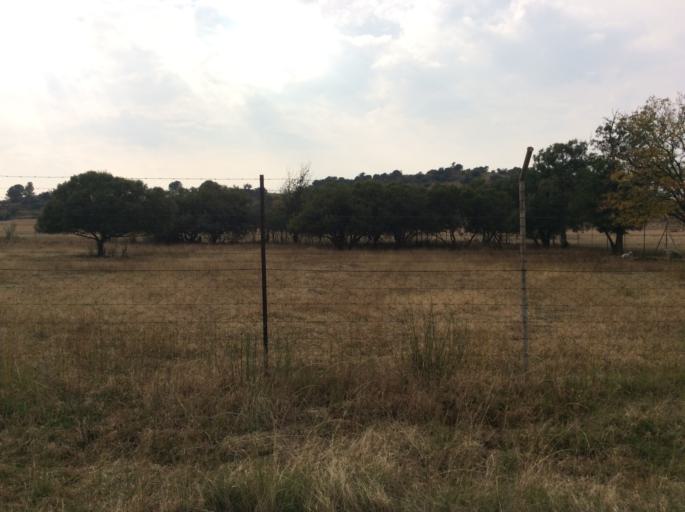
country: LS
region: Mafeteng
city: Mafeteng
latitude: -29.9900
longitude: 27.0201
